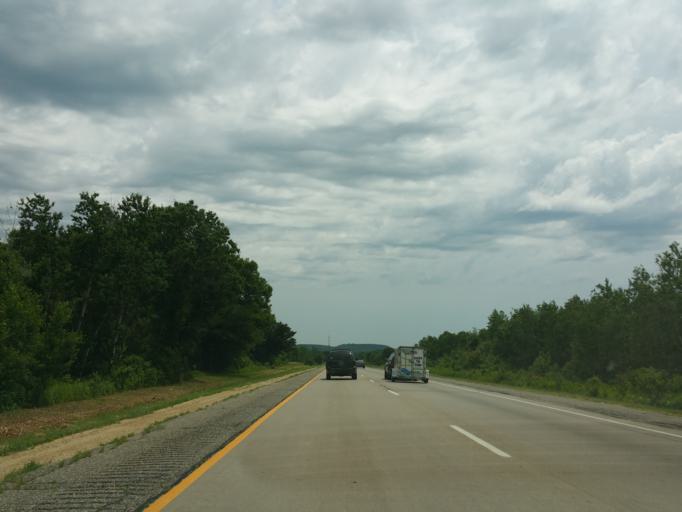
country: US
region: Wisconsin
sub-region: Columbia County
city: Wisconsin Dells
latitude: 43.6958
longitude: -89.8582
